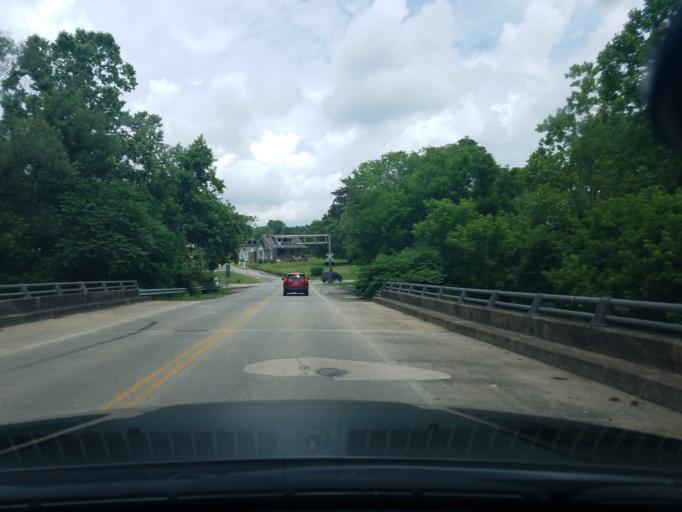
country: US
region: Pennsylvania
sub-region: Westmoreland County
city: Youngwood
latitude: 40.2273
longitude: -79.5884
